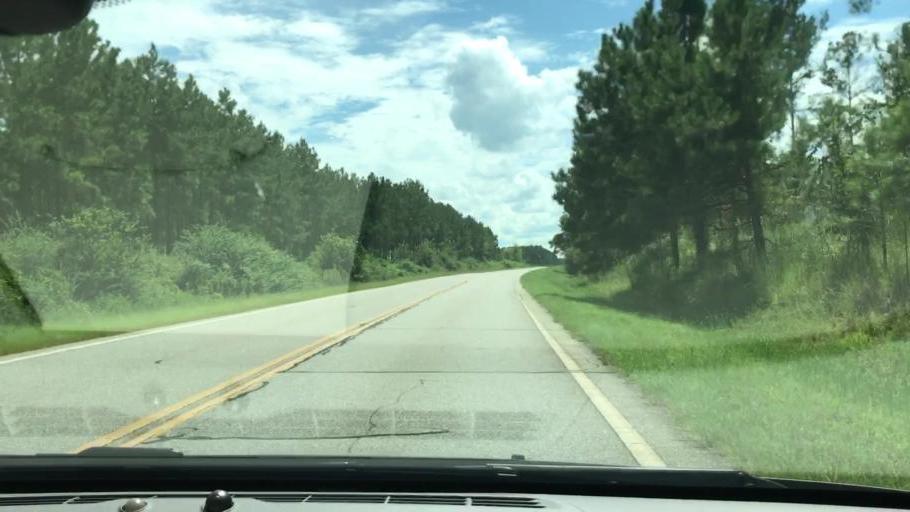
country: US
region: Georgia
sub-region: Quitman County
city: Georgetown
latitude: 32.0693
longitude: -85.0362
